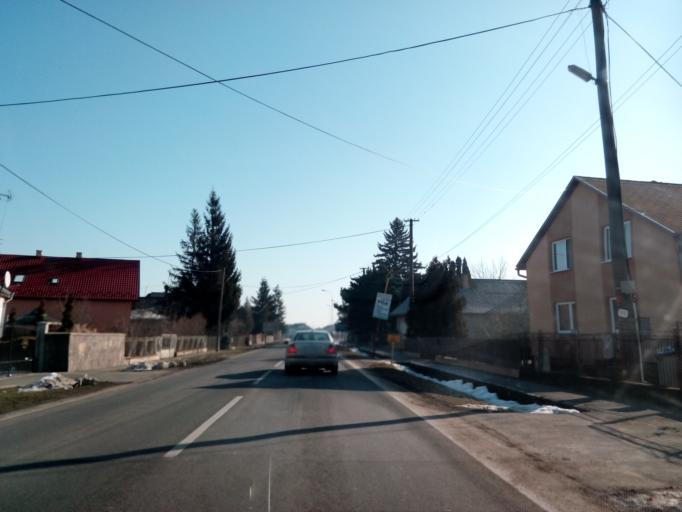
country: SK
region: Kosicky
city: Secovce
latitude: 48.7000
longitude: 21.7039
